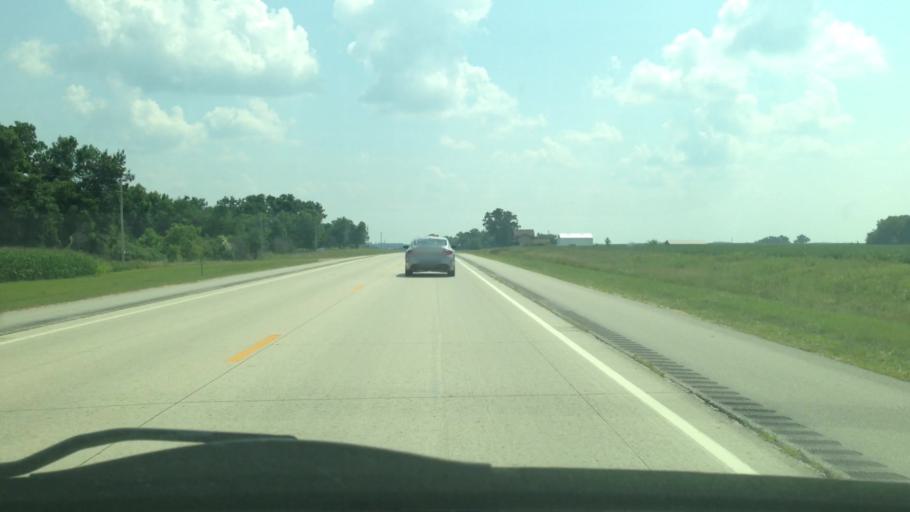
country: US
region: Minnesota
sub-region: Fillmore County
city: Spring Valley
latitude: 43.5194
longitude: -92.3694
